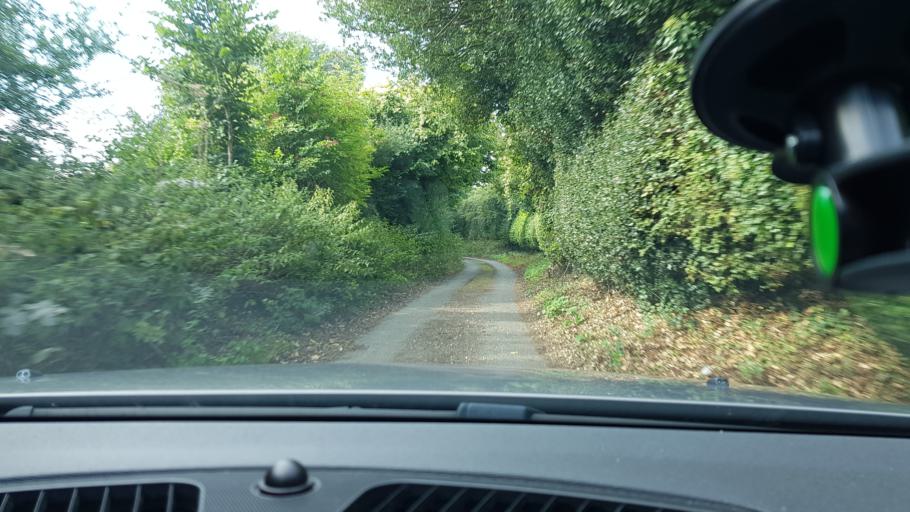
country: GB
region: England
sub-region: West Berkshire
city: Wickham
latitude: 51.4328
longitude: -1.4531
